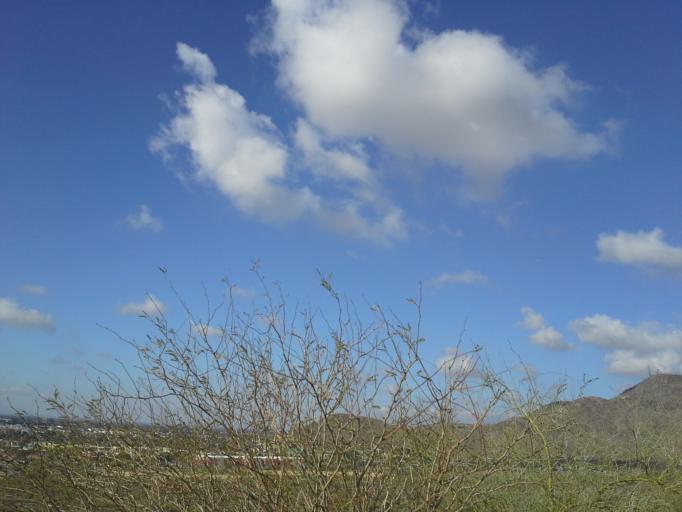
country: US
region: Arizona
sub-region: Maricopa County
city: Glendale
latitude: 33.5778
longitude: -112.0755
